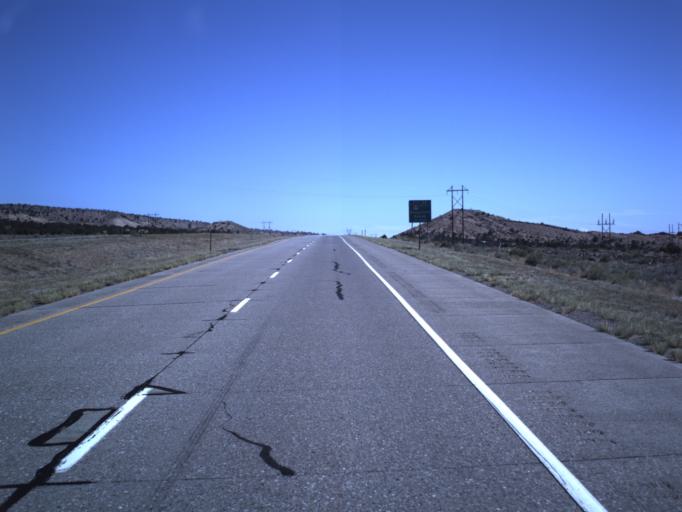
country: US
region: Utah
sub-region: Sevier County
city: Monroe
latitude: 38.5913
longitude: -112.2685
